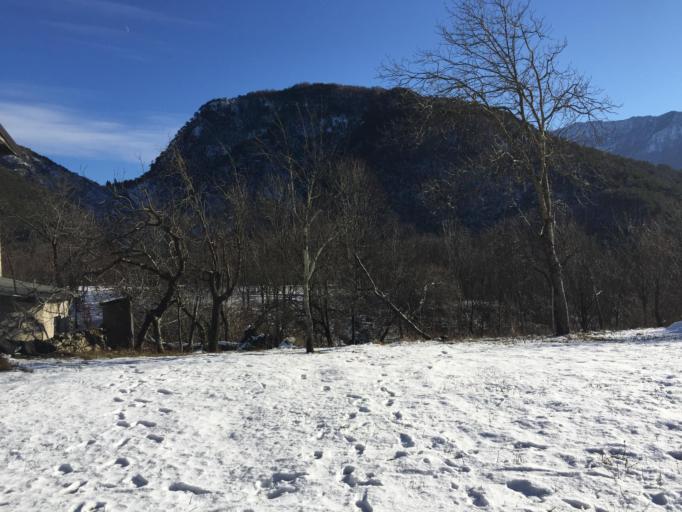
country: IT
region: Friuli Venezia Giulia
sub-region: Provincia di Udine
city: Moggio di Sotto
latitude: 46.4174
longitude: 13.1522
